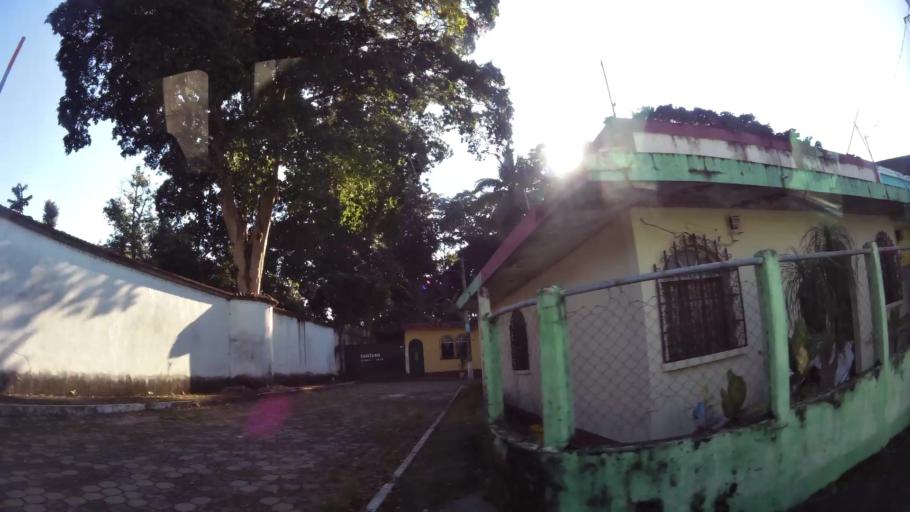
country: GT
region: Suchitepeque
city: Mazatenango
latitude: 14.5315
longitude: -91.5145
